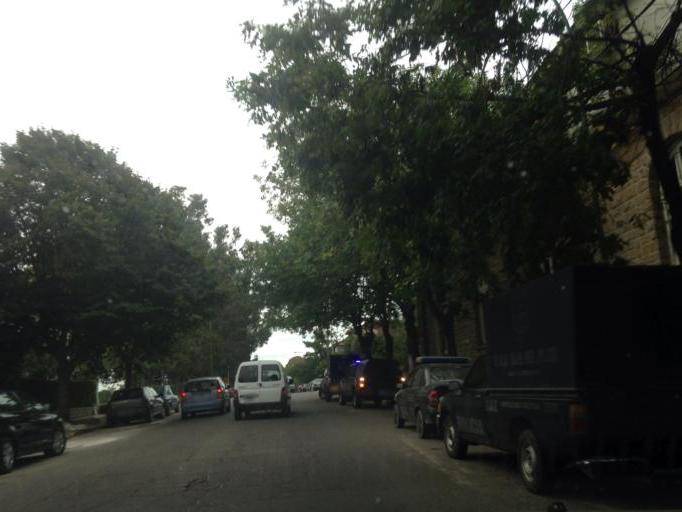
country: AR
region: Buenos Aires
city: Mar del Plata
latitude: -38.0220
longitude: -57.5566
